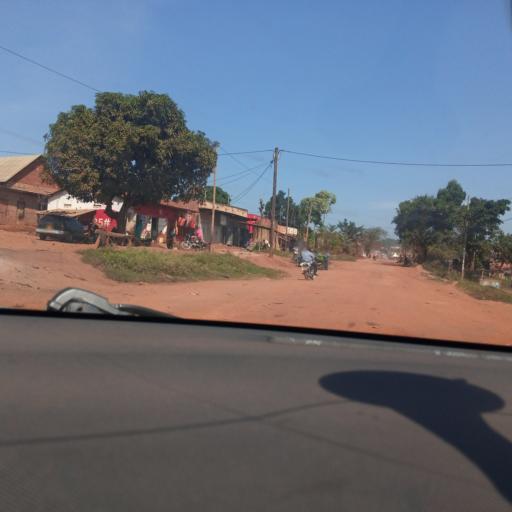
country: UG
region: Central Region
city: Masaka
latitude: -0.3097
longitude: 31.7567
